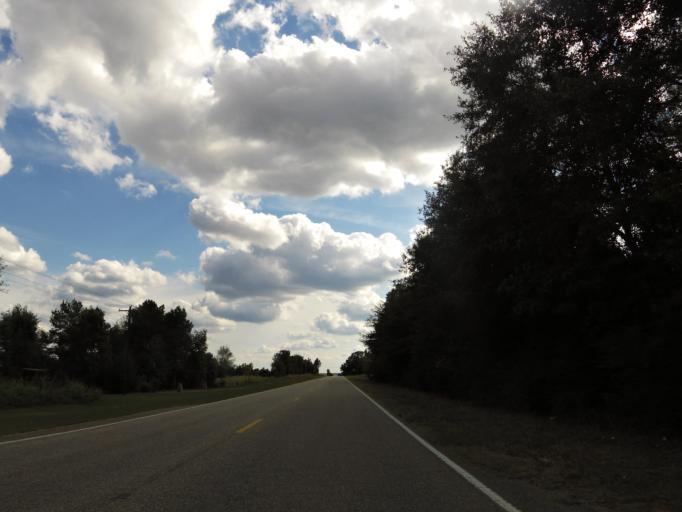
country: US
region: Alabama
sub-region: Dallas County
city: Selmont-West Selmont
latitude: 32.2618
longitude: -86.9908
